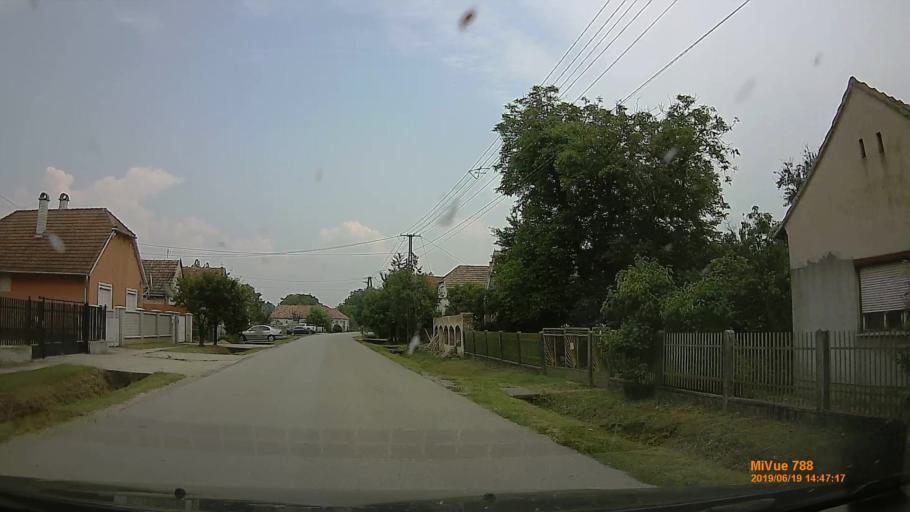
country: HU
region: Baranya
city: Szigetvar
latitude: 45.9978
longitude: 17.8300
